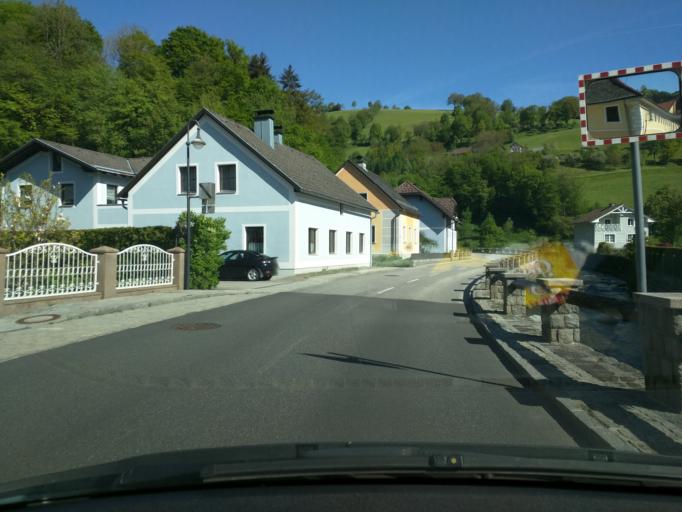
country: AT
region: Lower Austria
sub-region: Politischer Bezirk Scheibbs
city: Randegg
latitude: 48.0128
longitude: 14.9724
